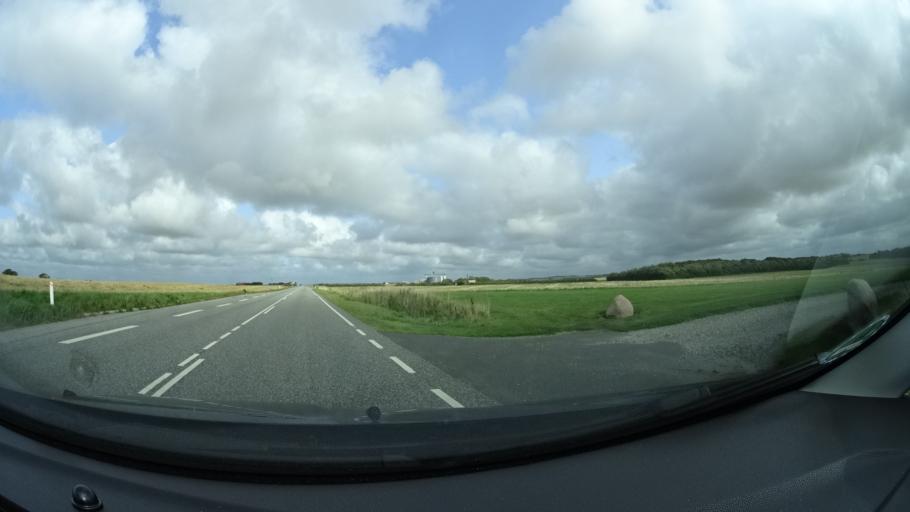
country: DK
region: Central Jutland
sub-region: Lemvig Kommune
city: Harboore
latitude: 56.5525
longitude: 8.1838
